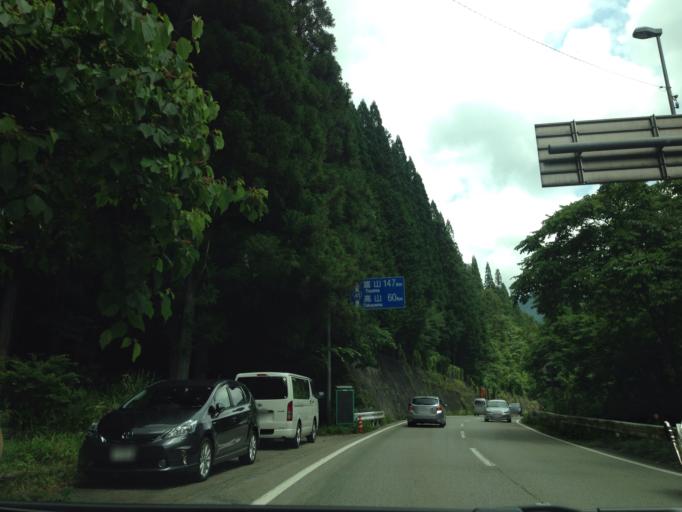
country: JP
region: Gifu
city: Gujo
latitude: 35.7587
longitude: 137.2254
